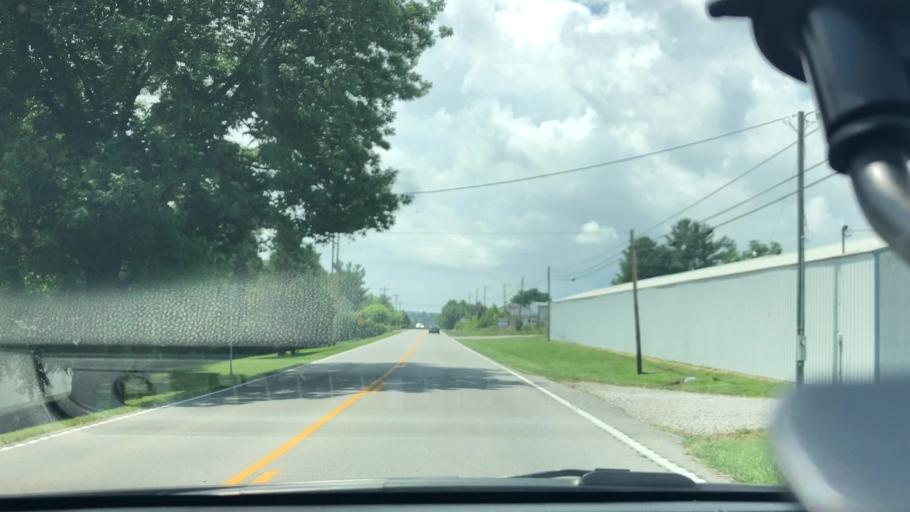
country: US
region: Kentucky
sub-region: Pulaski County
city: Somerset
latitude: 37.0616
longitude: -84.6754
